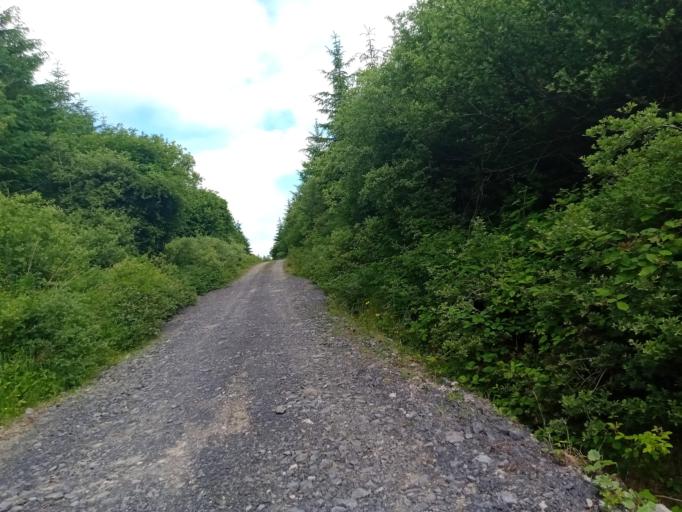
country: IE
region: Leinster
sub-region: Kilkenny
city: Ballyragget
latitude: 52.7888
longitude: -7.4466
